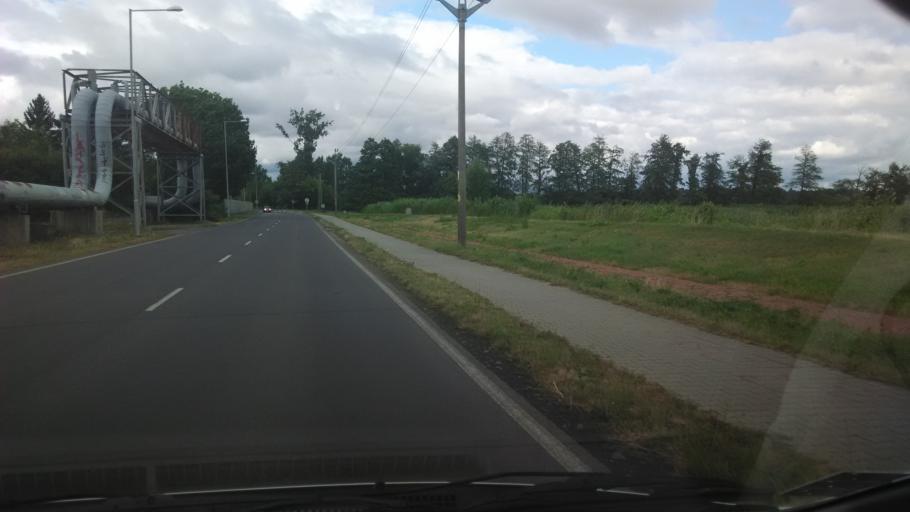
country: SK
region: Nitriansky
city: Levice
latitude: 48.2004
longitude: 18.6063
